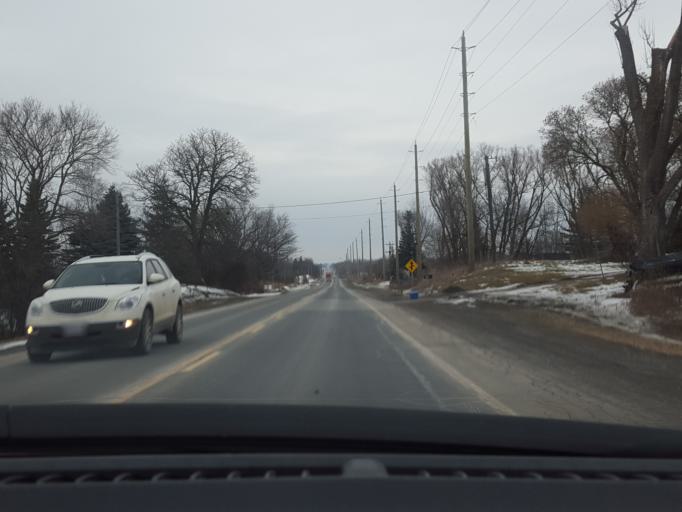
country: CA
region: Ontario
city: Keswick
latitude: 44.1770
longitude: -79.4342
